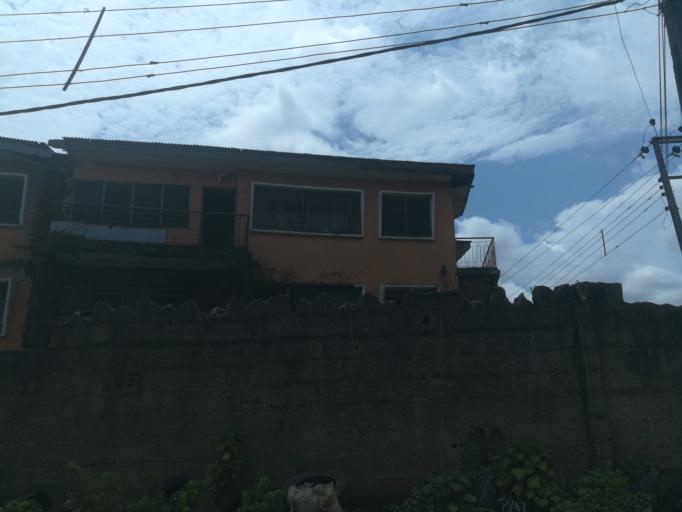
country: NG
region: Lagos
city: Somolu
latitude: 6.5245
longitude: 3.3844
